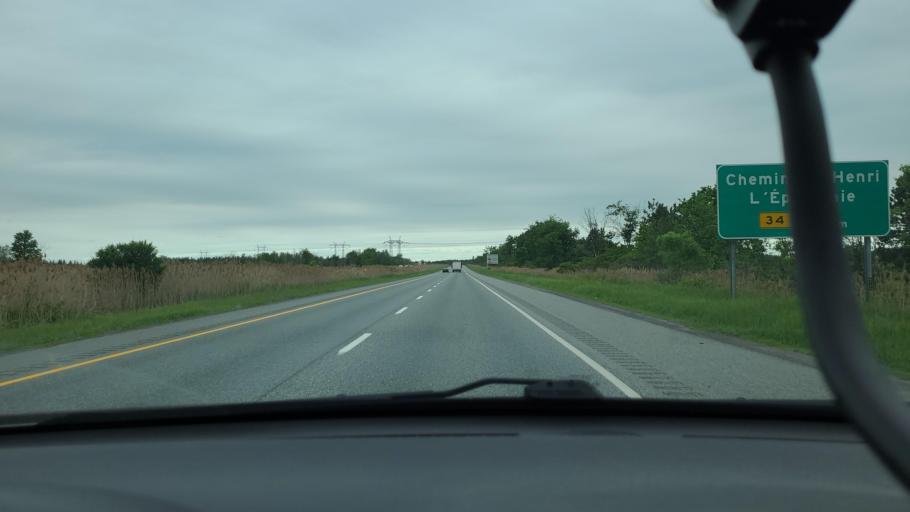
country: CA
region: Quebec
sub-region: Lanaudiere
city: Mascouche
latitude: 45.7689
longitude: -73.5763
